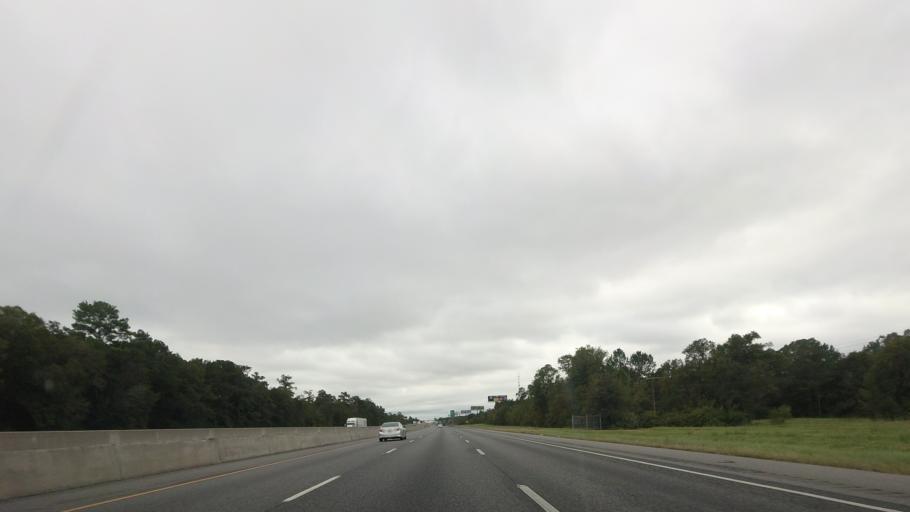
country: US
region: Georgia
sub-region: Lowndes County
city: Hahira
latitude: 31.0050
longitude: -83.3920
